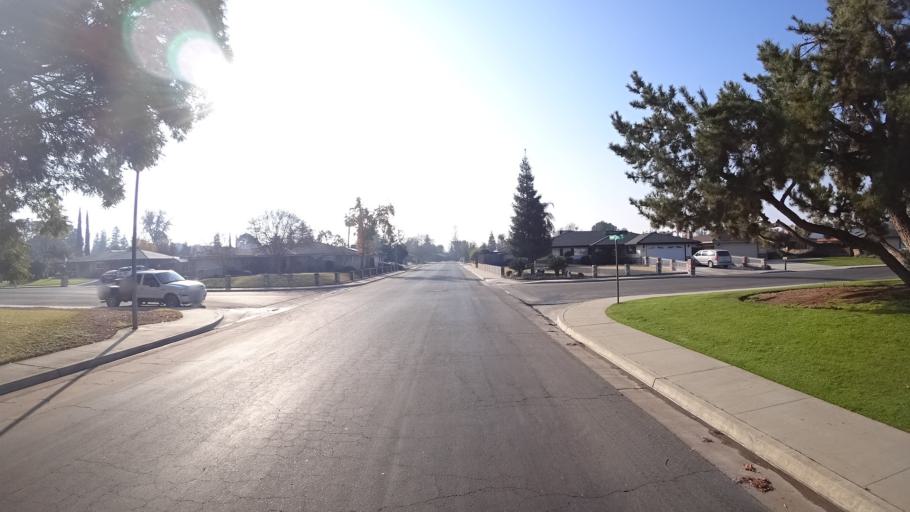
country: US
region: California
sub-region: Kern County
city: Greenacres
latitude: 35.3386
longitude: -119.0757
